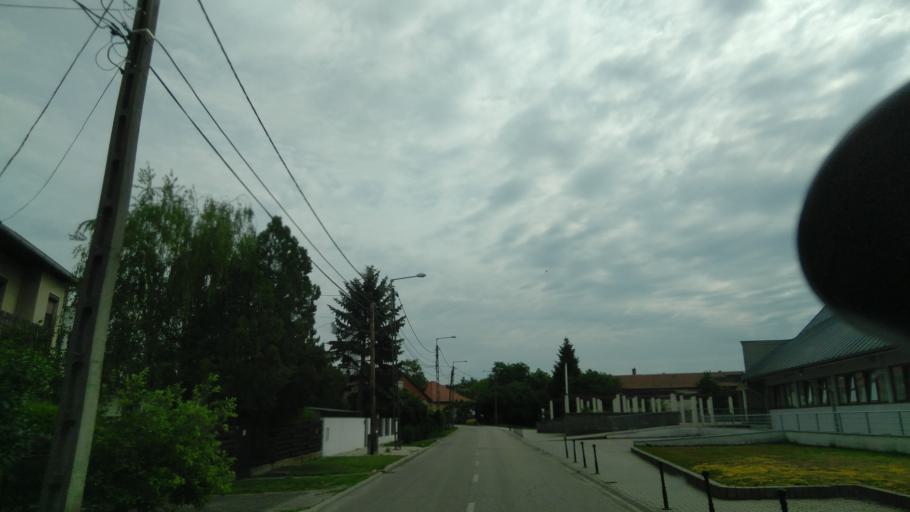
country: HU
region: Bekes
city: Szeghalom
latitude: 47.0136
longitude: 21.1721
